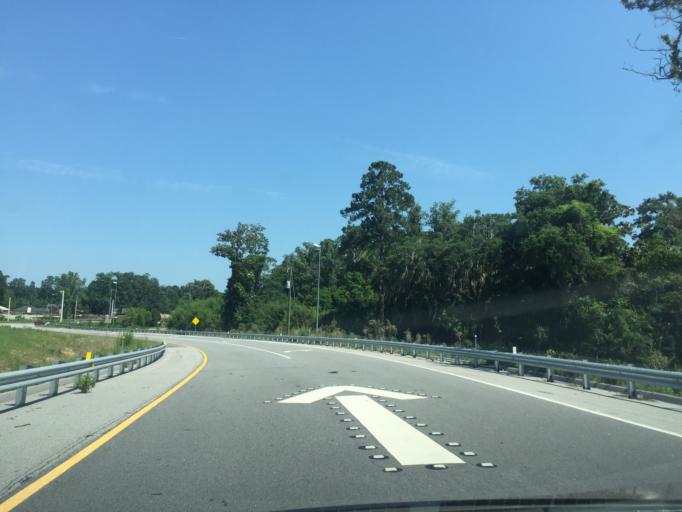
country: US
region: Georgia
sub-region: Chatham County
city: Montgomery
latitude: 31.9729
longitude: -81.1073
